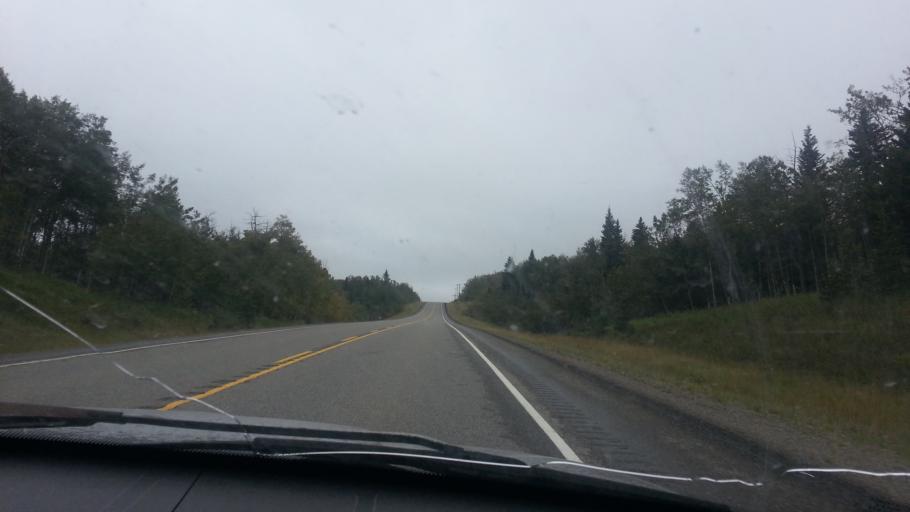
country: CA
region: Alberta
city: Cochrane
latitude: 51.0929
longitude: -114.6993
